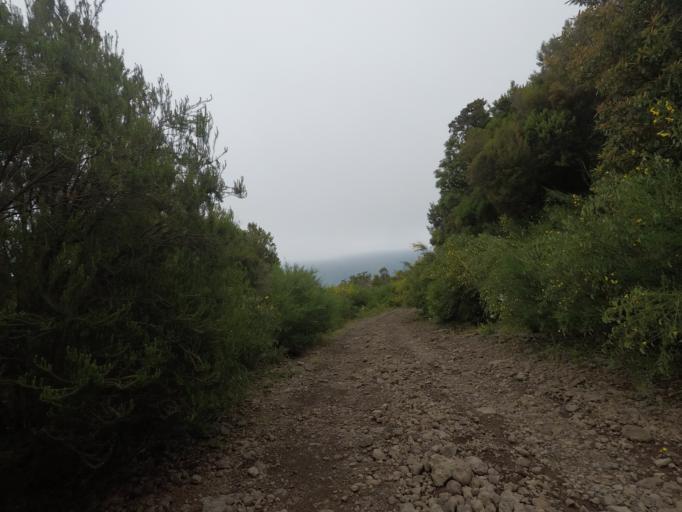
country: PT
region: Madeira
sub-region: Sao Vicente
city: Sao Vicente
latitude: 32.7727
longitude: -17.0575
